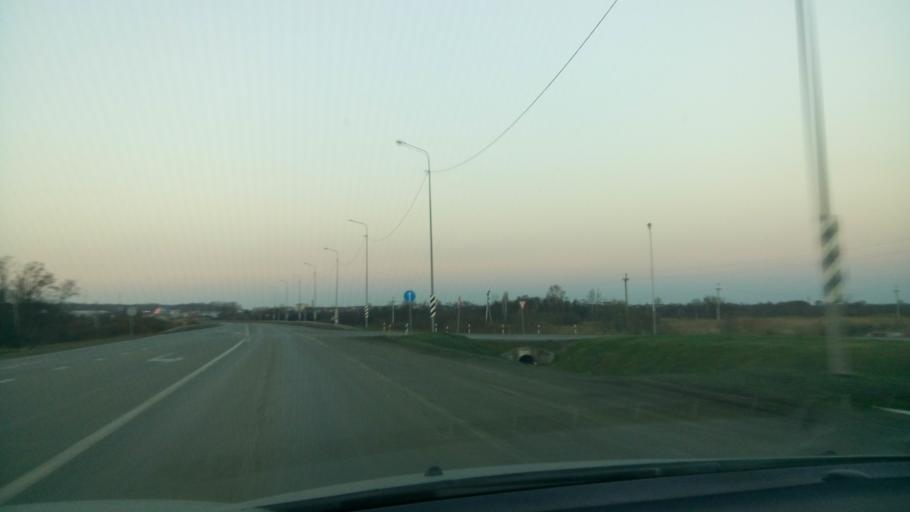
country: RU
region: Sverdlovsk
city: Pyshma
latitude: 56.9413
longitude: 63.2171
